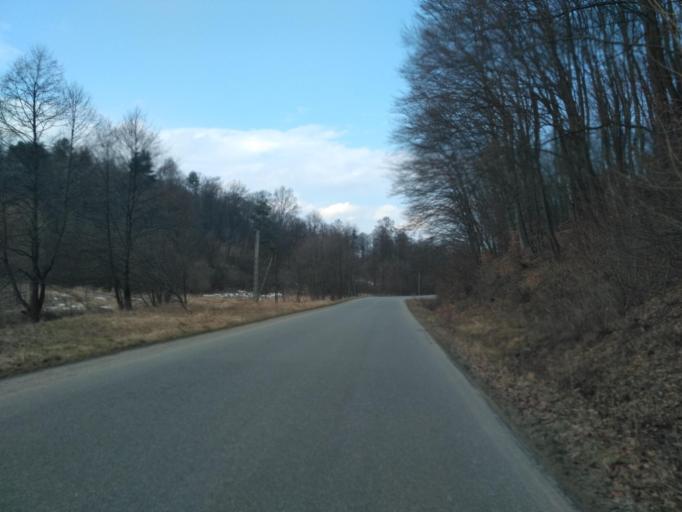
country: PL
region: Subcarpathian Voivodeship
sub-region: Powiat brzozowski
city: Gorki
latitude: 49.6357
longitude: 22.0564
